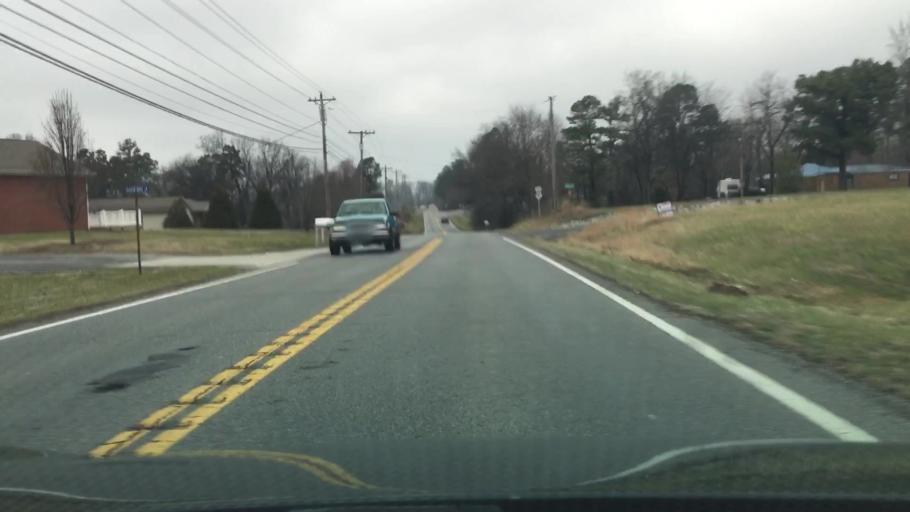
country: US
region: Kentucky
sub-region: Marshall County
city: Benton
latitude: 36.9444
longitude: -88.3638
